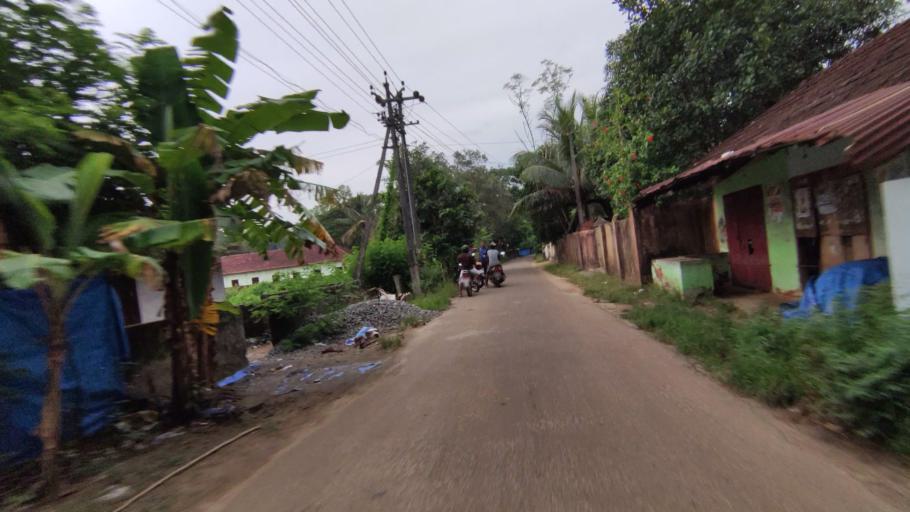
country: IN
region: Kerala
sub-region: Alappuzha
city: Shertallai
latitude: 9.6502
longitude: 76.3675
